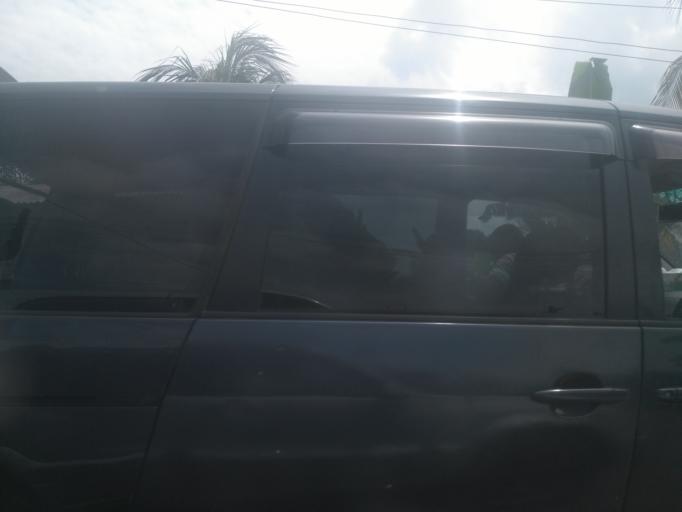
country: TZ
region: Zanzibar Urban/West
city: Zanzibar
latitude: -6.2351
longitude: 39.2131
